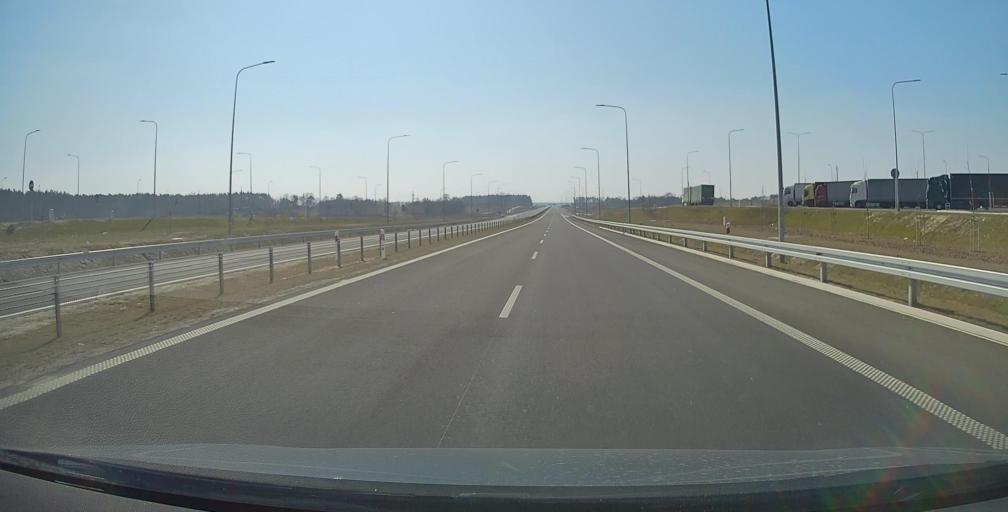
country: PL
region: Lublin Voivodeship
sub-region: Powiat janowski
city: Modliborzyce
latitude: 50.7818
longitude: 22.2914
